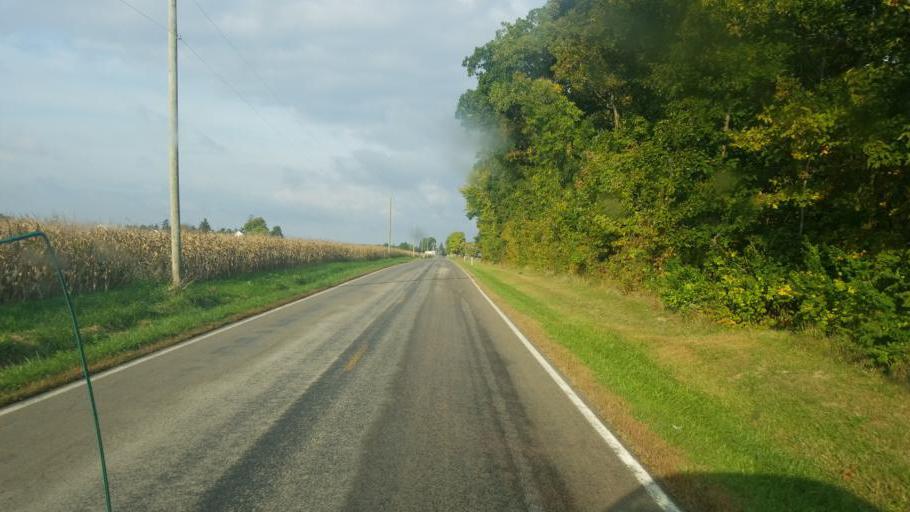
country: US
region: Ohio
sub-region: Wyandot County
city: Upper Sandusky
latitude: 40.8614
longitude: -83.3535
